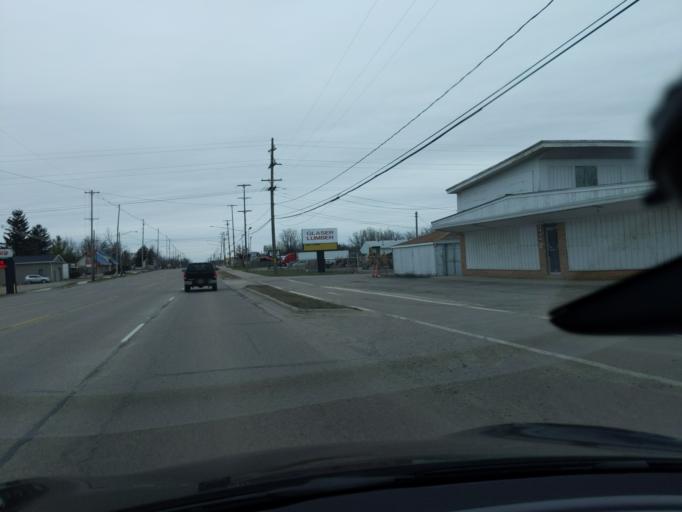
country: US
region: Michigan
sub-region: Ingham County
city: Lansing
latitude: 42.7765
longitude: -84.5426
